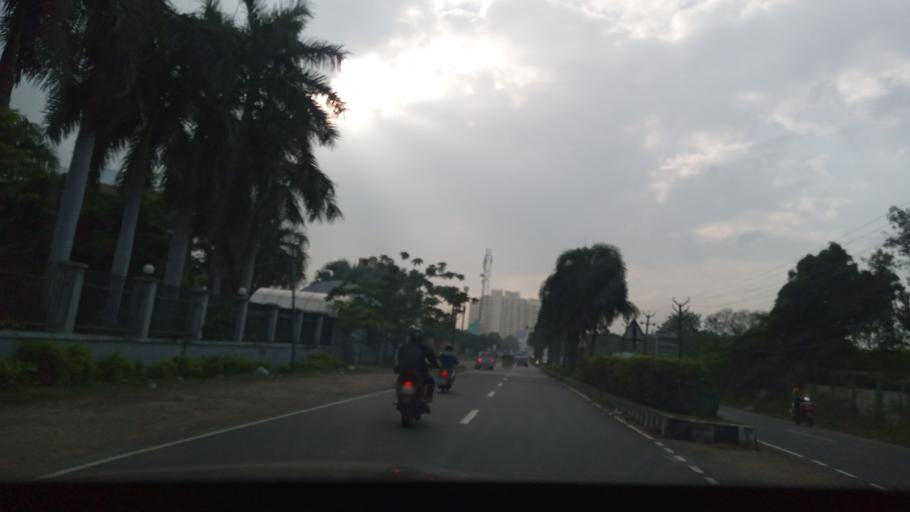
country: IN
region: Tamil Nadu
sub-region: Kancheepuram
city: Vengavasal
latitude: 12.8410
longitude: 80.1521
